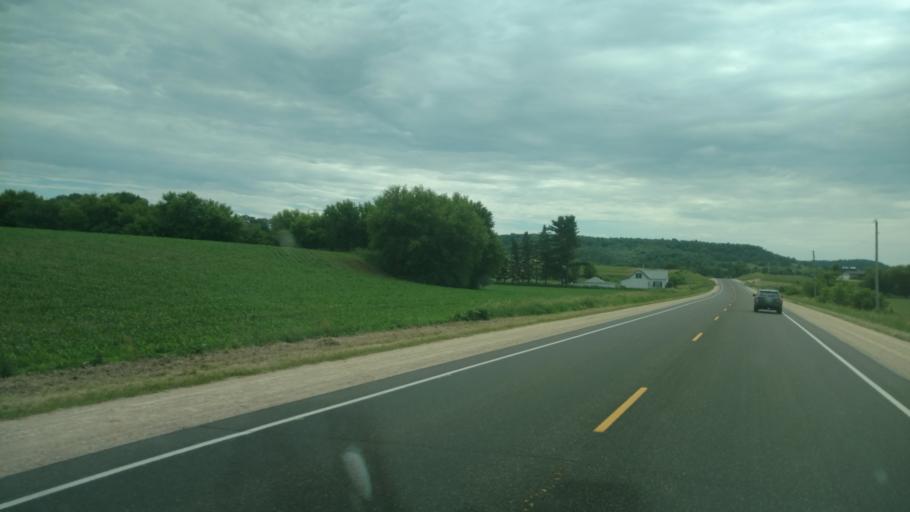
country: US
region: Wisconsin
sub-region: Monroe County
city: Tomah
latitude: 43.8419
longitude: -90.4739
